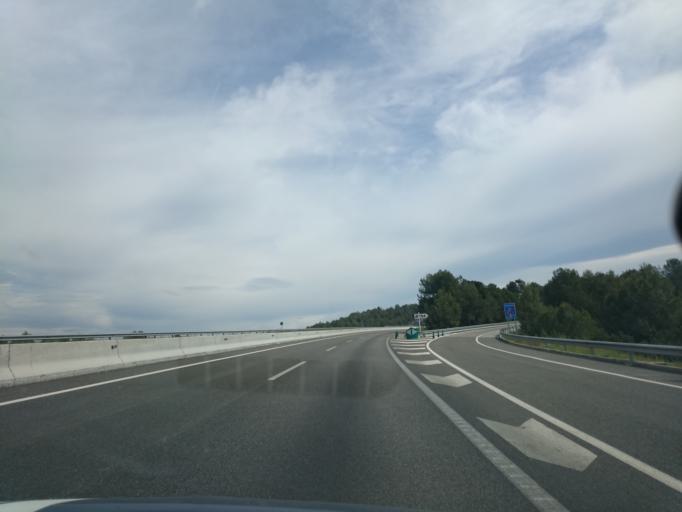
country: ES
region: Catalonia
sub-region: Provincia de Barcelona
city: Avinyo
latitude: 41.8534
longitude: 1.9833
